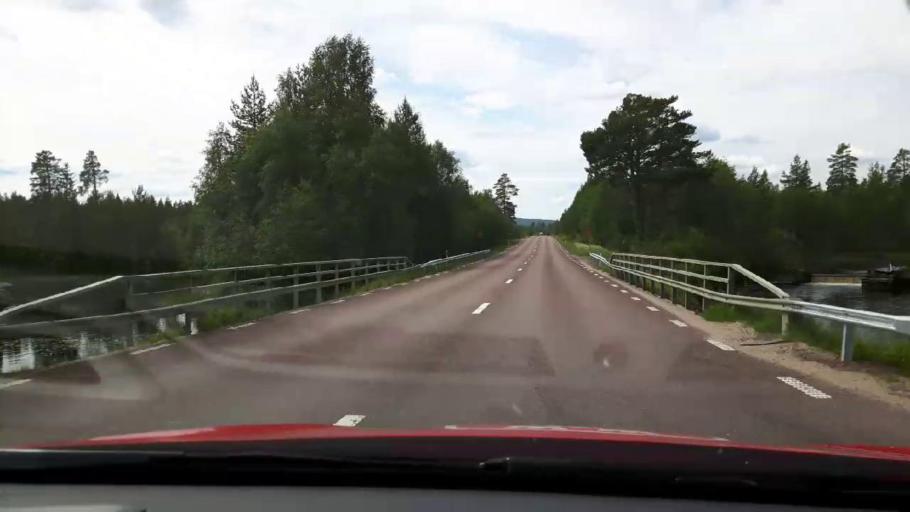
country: SE
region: Jaemtland
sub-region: Harjedalens Kommun
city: Sveg
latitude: 62.0449
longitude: 14.4742
